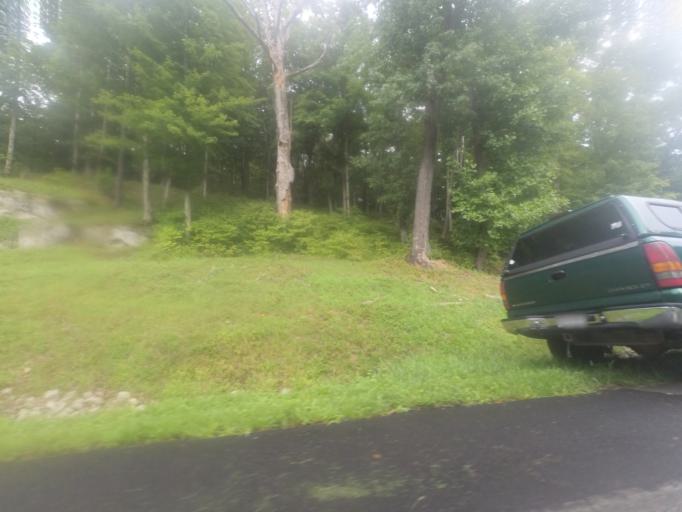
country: US
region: West Virginia
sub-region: Cabell County
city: Huntington
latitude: 38.3870
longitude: -82.4057
